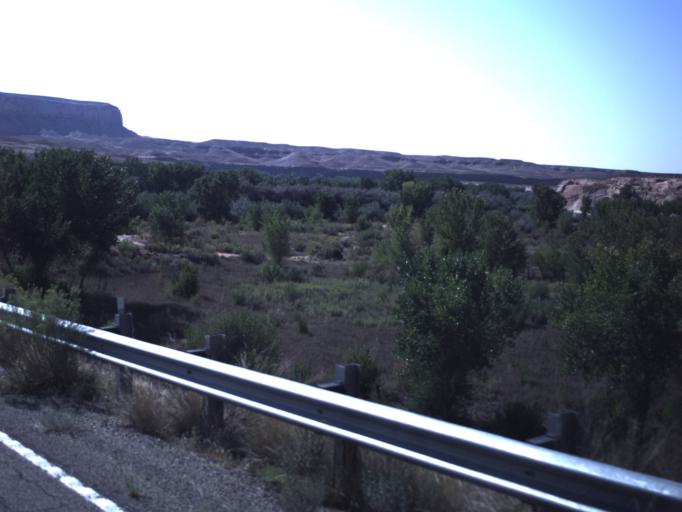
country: US
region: Utah
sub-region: San Juan County
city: Blanding
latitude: 37.2594
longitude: -109.6206
